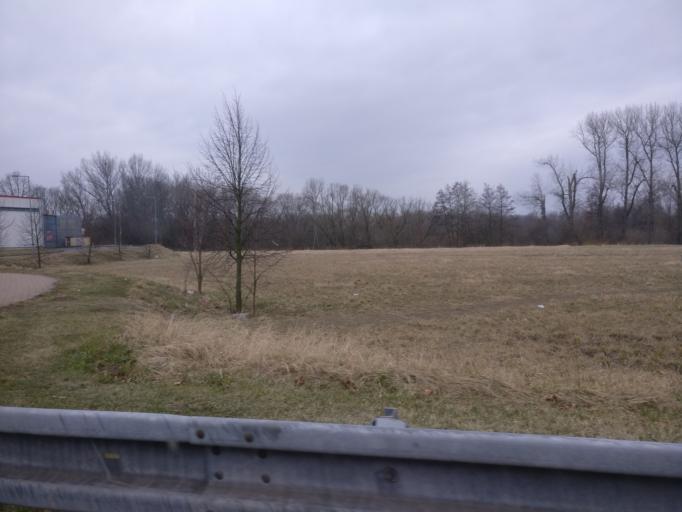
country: CZ
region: Pardubicky
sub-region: Okres Pardubice
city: Pardubice
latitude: 50.0374
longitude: 15.7533
